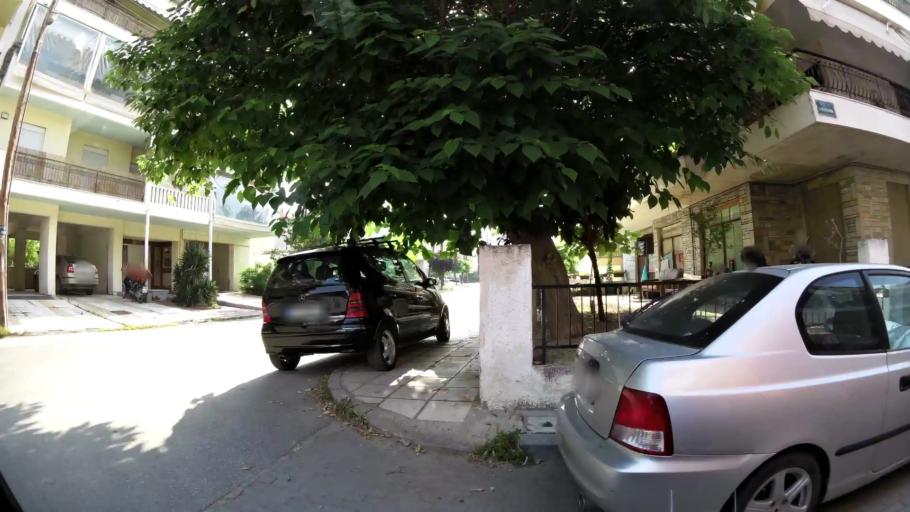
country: GR
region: Central Macedonia
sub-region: Nomos Thessalonikis
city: Evosmos
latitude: 40.6636
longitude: 22.9175
